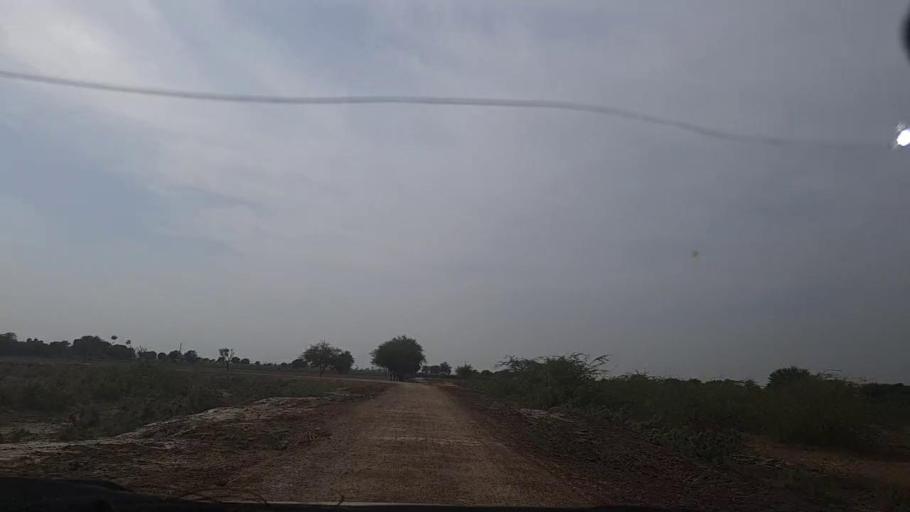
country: PK
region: Sindh
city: Pithoro
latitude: 25.5475
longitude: 69.3567
